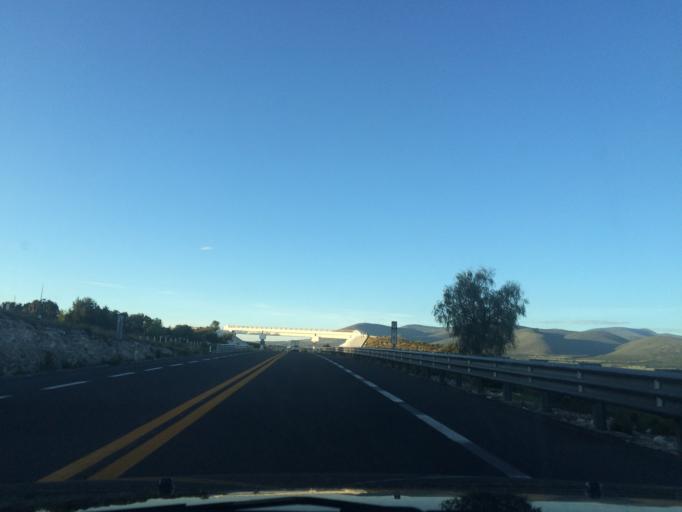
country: MX
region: Puebla
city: Cuacnopalan
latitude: 18.7832
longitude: -97.4881
